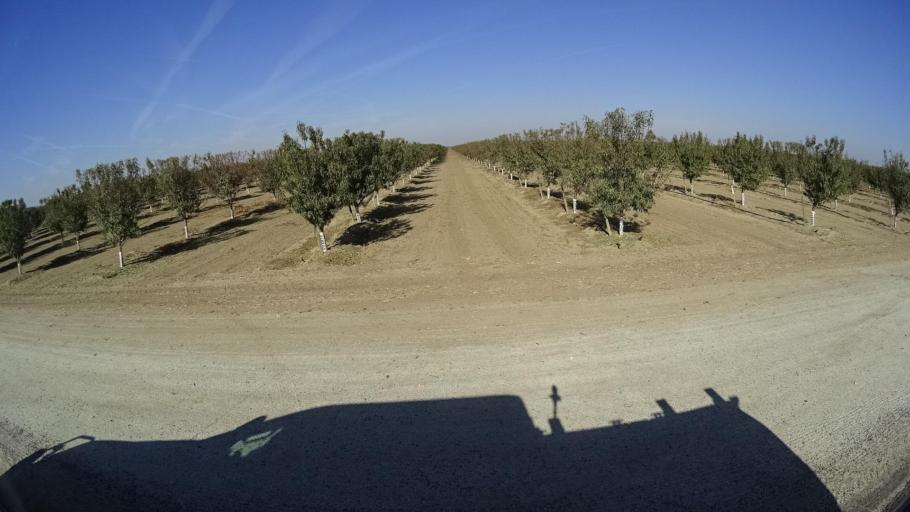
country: US
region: California
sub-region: Kern County
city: McFarland
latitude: 35.6455
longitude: -119.2256
